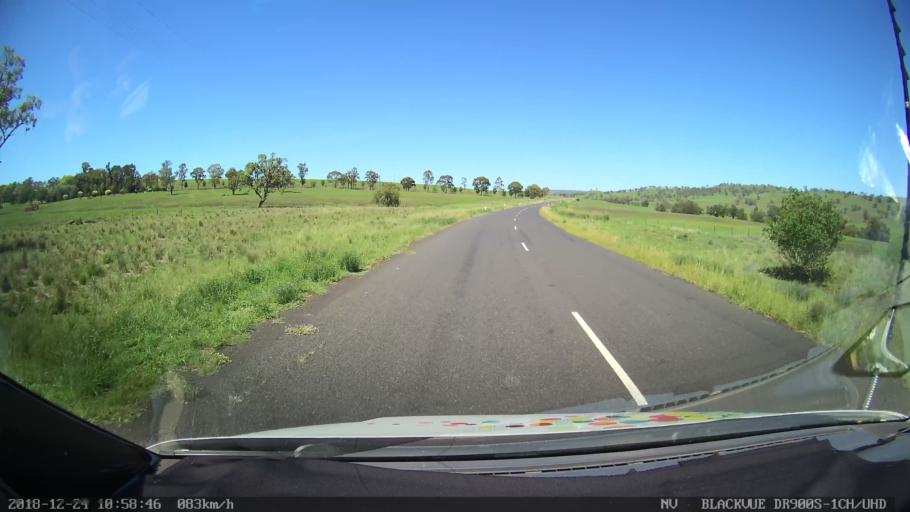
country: AU
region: New South Wales
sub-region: Upper Hunter Shire
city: Merriwa
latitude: -32.0512
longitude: 150.4047
